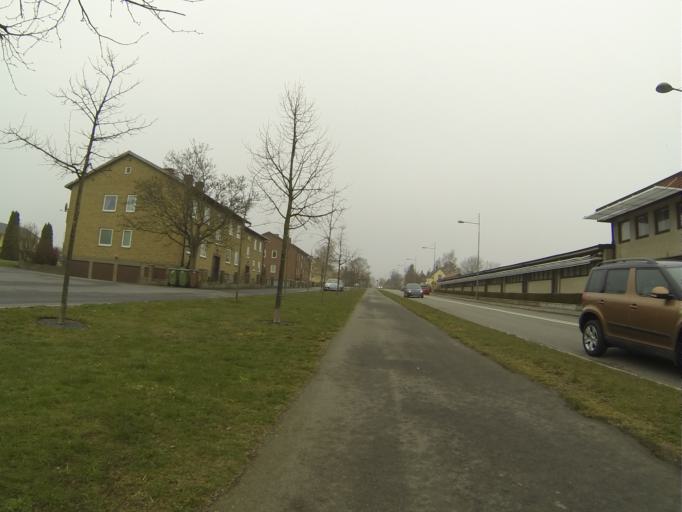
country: SE
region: Skane
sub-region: Simrishamns Kommun
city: Kivik
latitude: 55.5450
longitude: 14.1893
